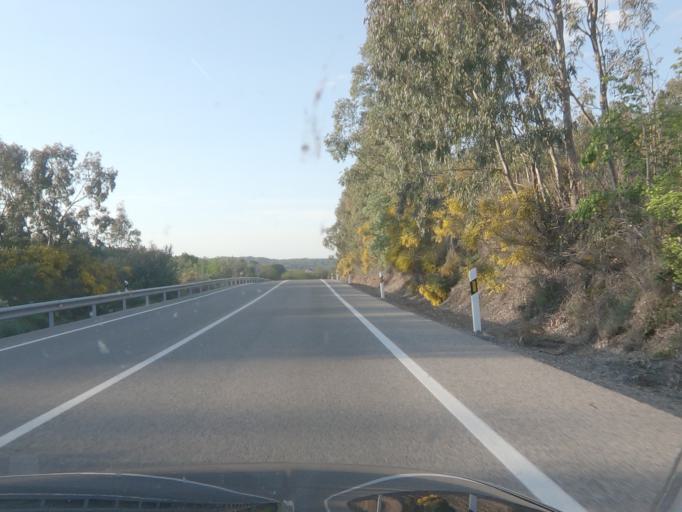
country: PT
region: Portalegre
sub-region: Portalegre
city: Sao Juliao
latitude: 39.3432
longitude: -7.2760
